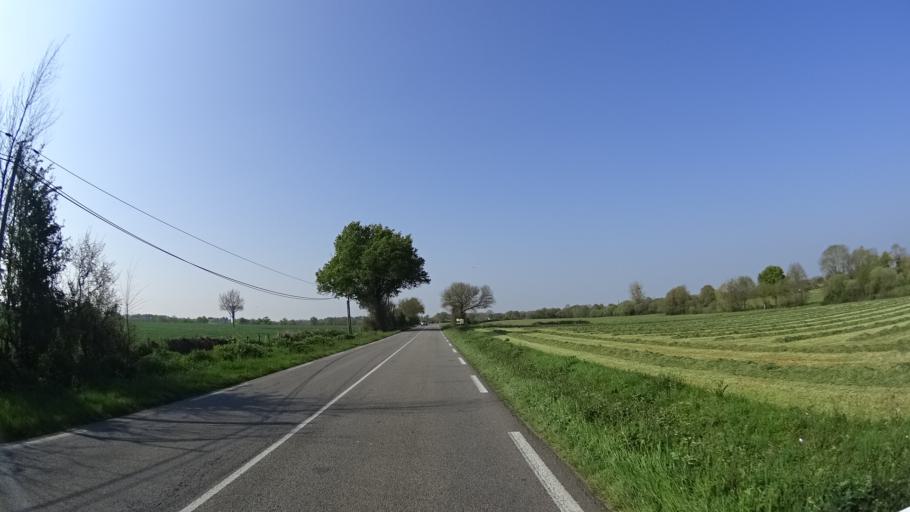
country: FR
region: Pays de la Loire
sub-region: Departement de la Loire-Atlantique
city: Sainte-Pazanne
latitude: 47.1128
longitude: -1.7788
